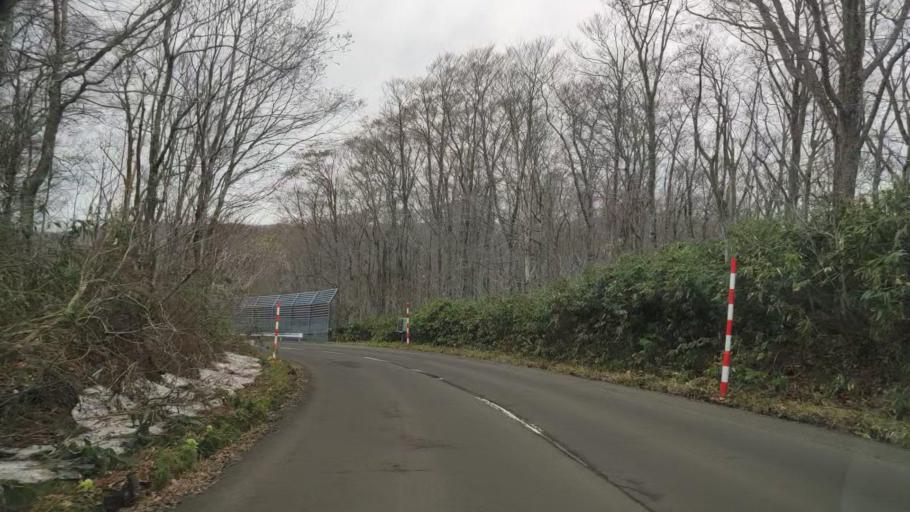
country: JP
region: Akita
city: Hanawa
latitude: 40.4185
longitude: 140.8226
